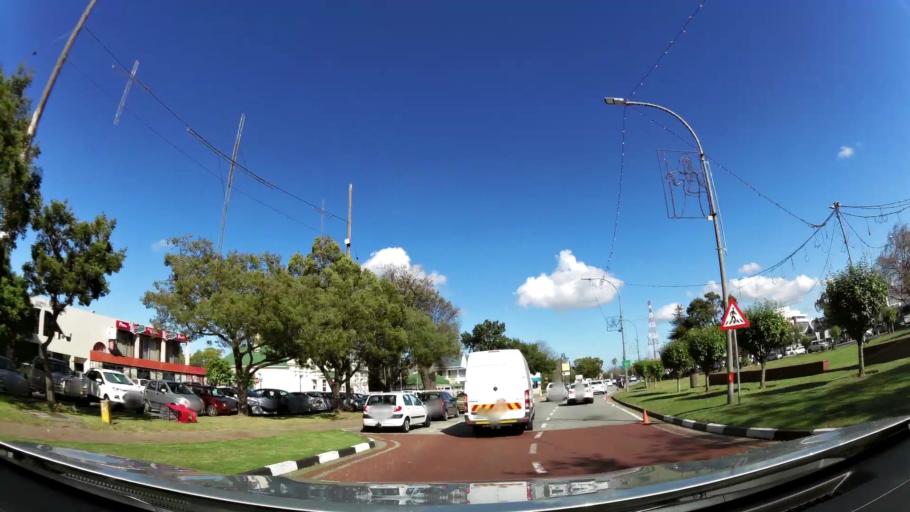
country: ZA
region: Western Cape
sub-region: Eden District Municipality
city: George
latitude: -33.9560
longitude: 22.4592
